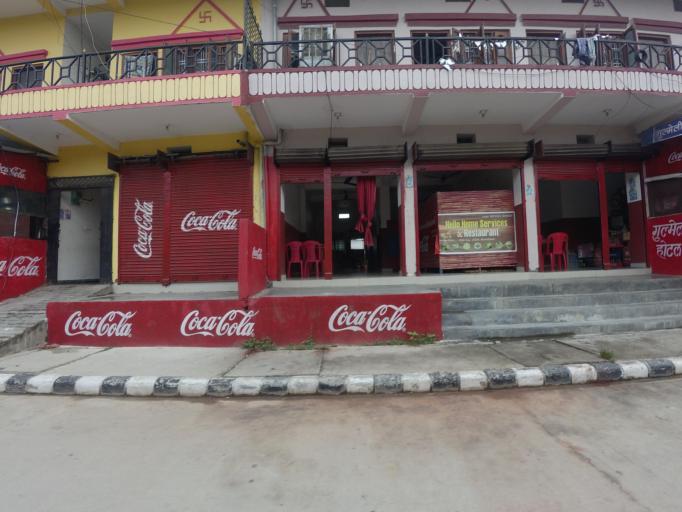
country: NP
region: Western Region
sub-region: Lumbini Zone
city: Bhairahawa
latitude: 27.4896
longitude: 83.4501
